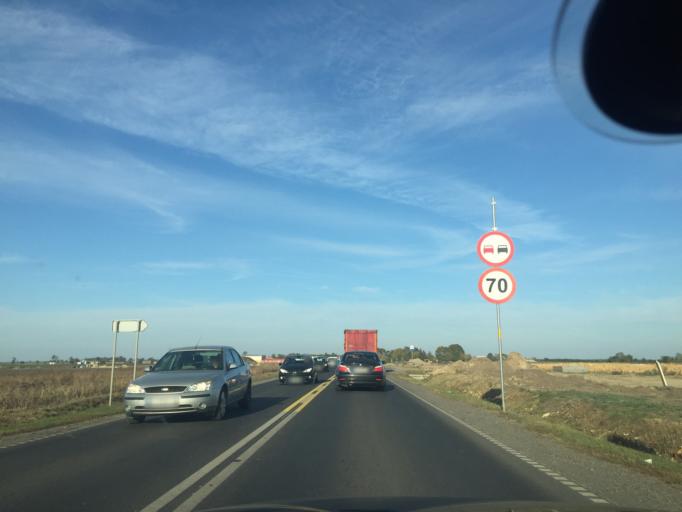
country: PL
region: Kujawsko-Pomorskie
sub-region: Powiat inowroclawski
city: Inowroclaw
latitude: 52.8159
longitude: 18.2902
